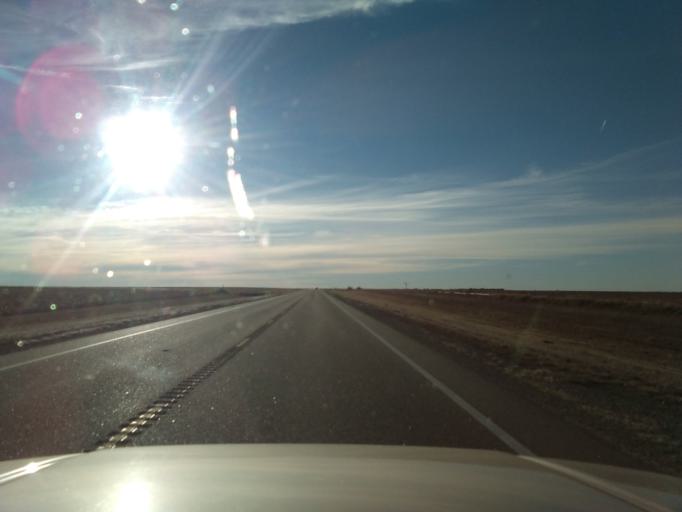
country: US
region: Kansas
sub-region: Sheridan County
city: Hoxie
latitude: 39.5233
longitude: -100.6160
